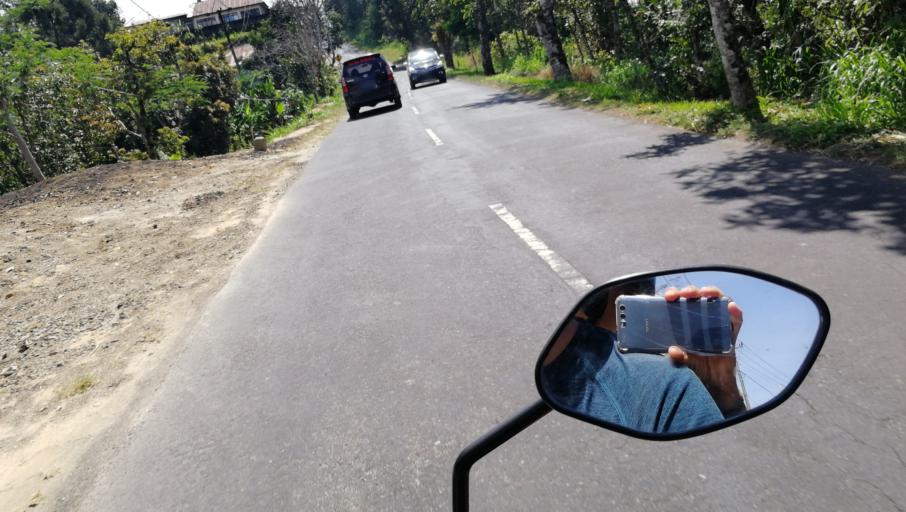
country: ID
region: Bali
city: Munduk
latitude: -8.2376
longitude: 115.1147
